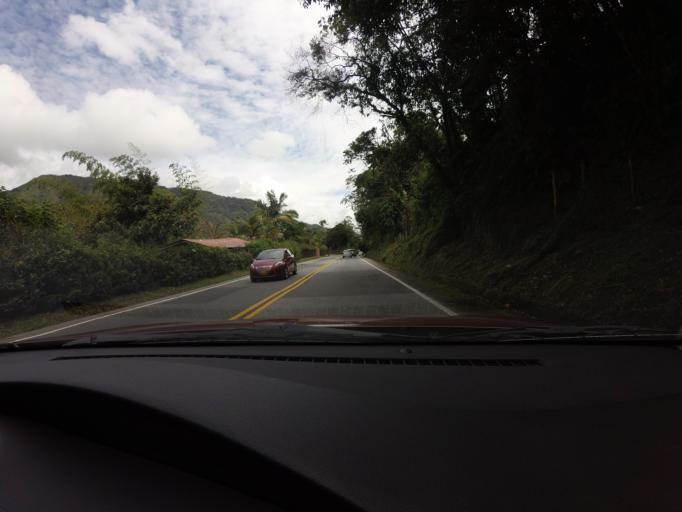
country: CO
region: Antioquia
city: Cocorna
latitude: 6.0416
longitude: -75.2224
